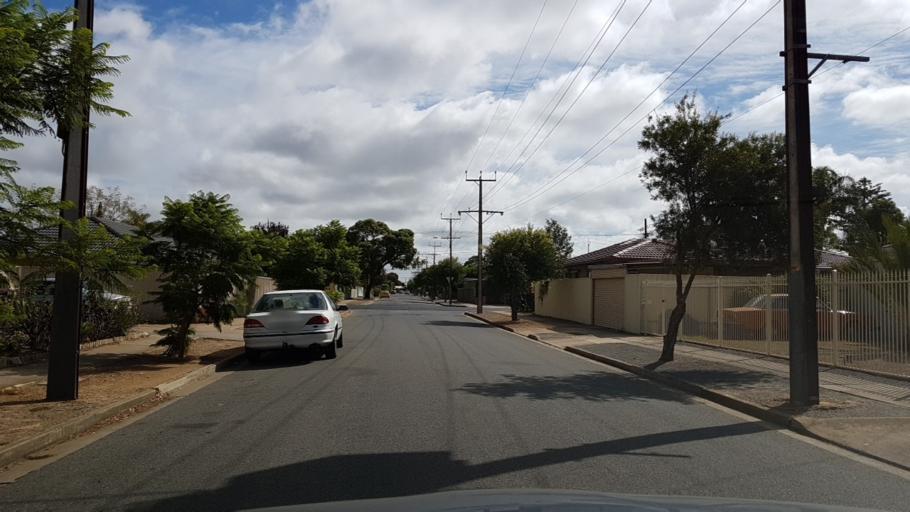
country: AU
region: South Australia
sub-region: Marion
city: Plympton Park
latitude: -34.9871
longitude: 138.5501
